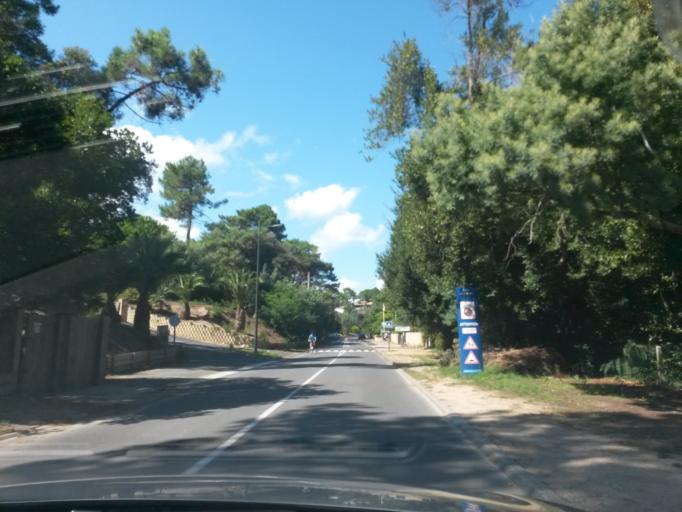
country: FR
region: Aquitaine
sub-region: Departement de la Gironde
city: Arcachon
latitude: 44.6717
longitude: -1.2408
